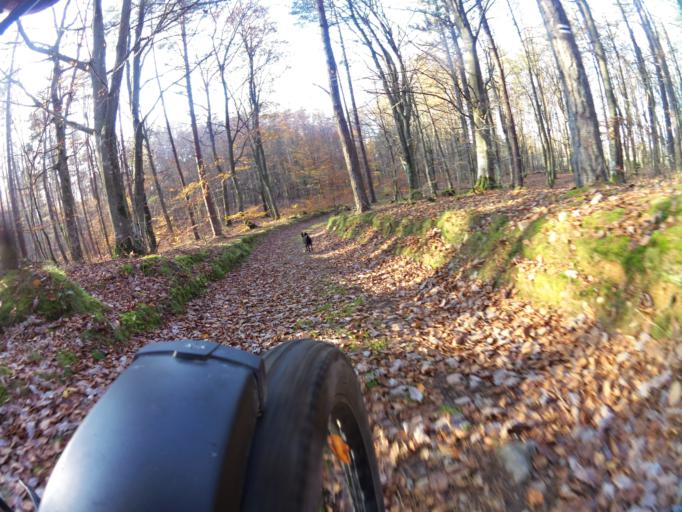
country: PL
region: Pomeranian Voivodeship
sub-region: Powiat pucki
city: Krokowa
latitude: 54.7293
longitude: 18.2006
